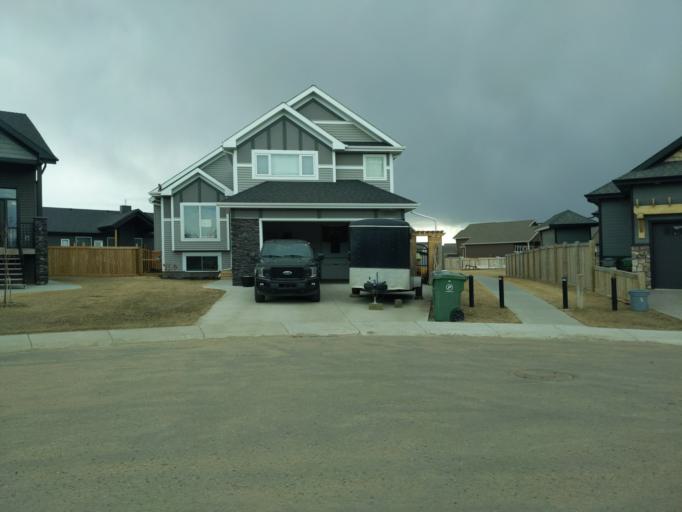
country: CA
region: Saskatchewan
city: Lloydminster
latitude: 53.2555
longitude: -110.0393
